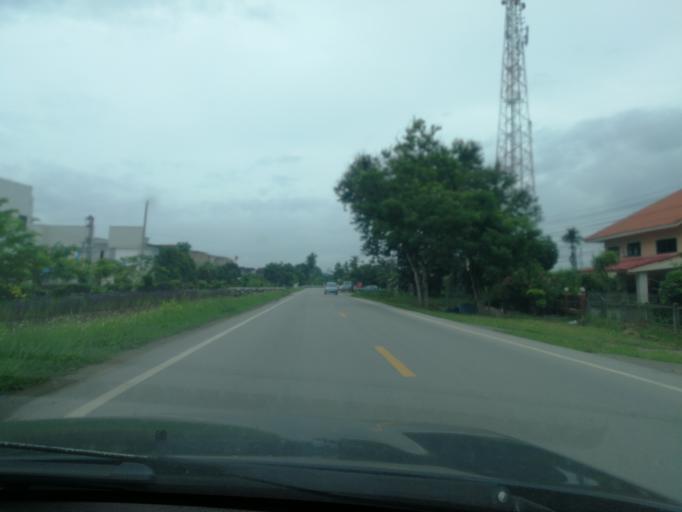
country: TH
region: Chiang Mai
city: San Pa Tong
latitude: 18.6202
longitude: 98.8972
